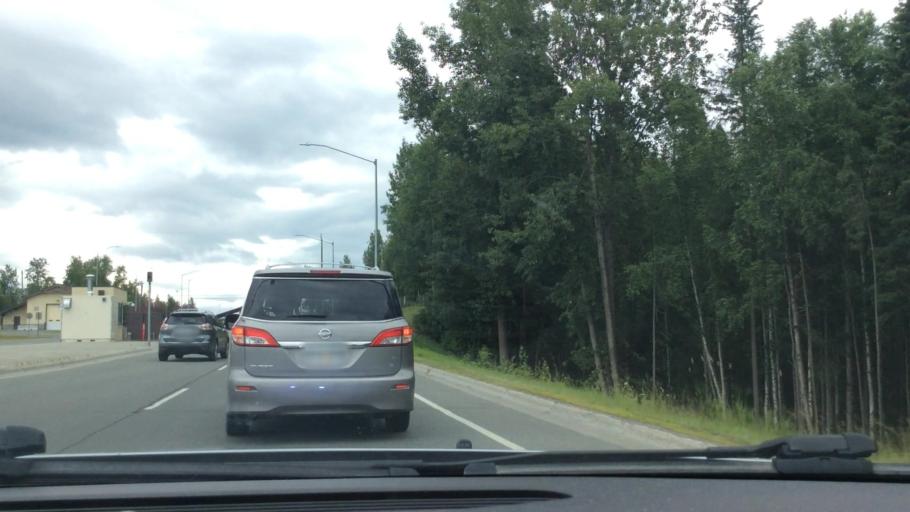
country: US
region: Alaska
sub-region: Anchorage Municipality
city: Anchorage
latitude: 61.2332
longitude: -149.7787
